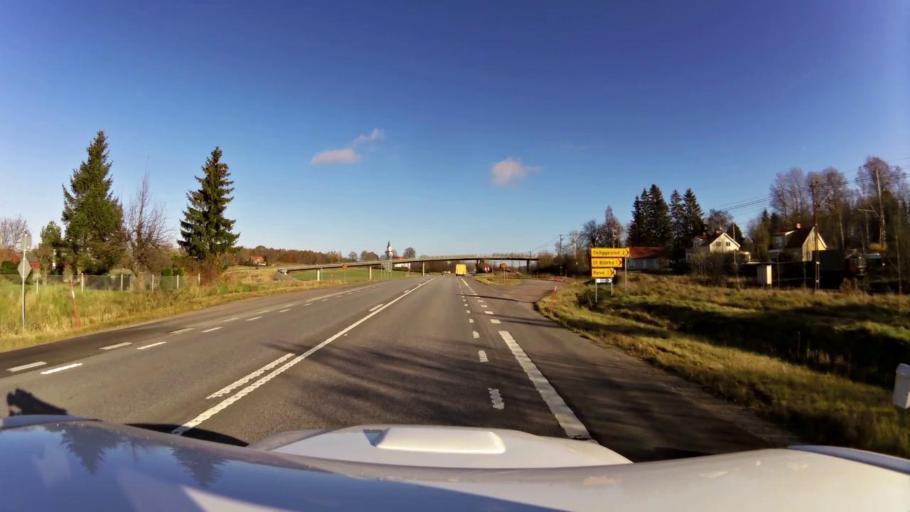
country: SE
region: OEstergoetland
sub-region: Linkopings Kommun
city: Linghem
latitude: 58.4479
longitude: 15.8235
